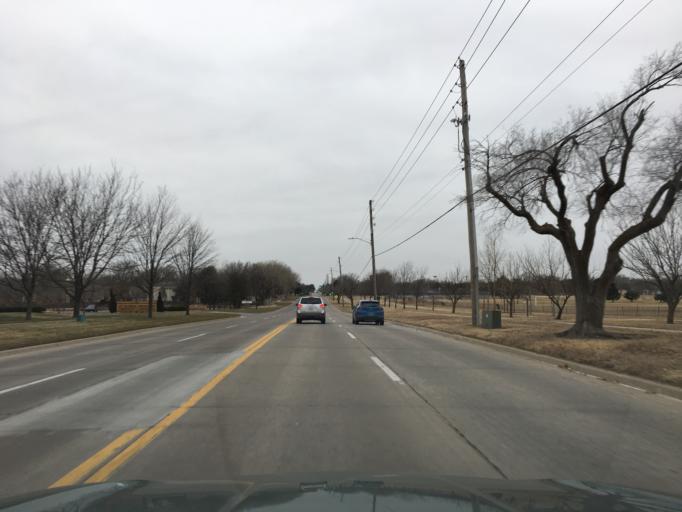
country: US
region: Kansas
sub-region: Sedgwick County
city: Bellaire
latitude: 37.7085
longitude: -97.2492
